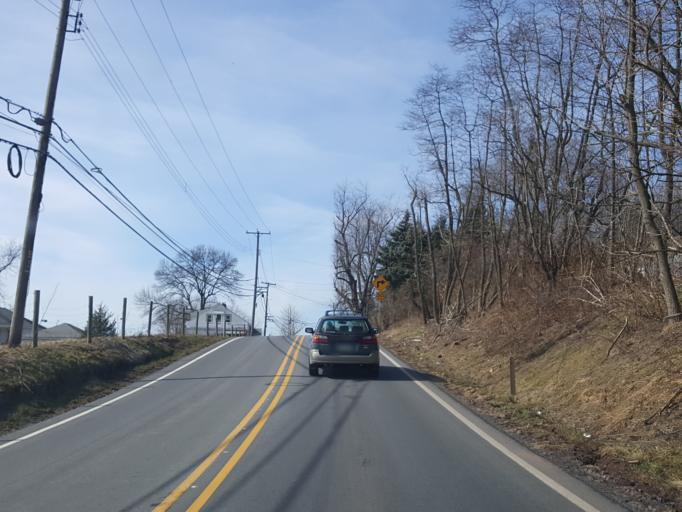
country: US
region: Pennsylvania
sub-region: Lebanon County
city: Campbelltown
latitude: 40.2706
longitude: -76.5633
